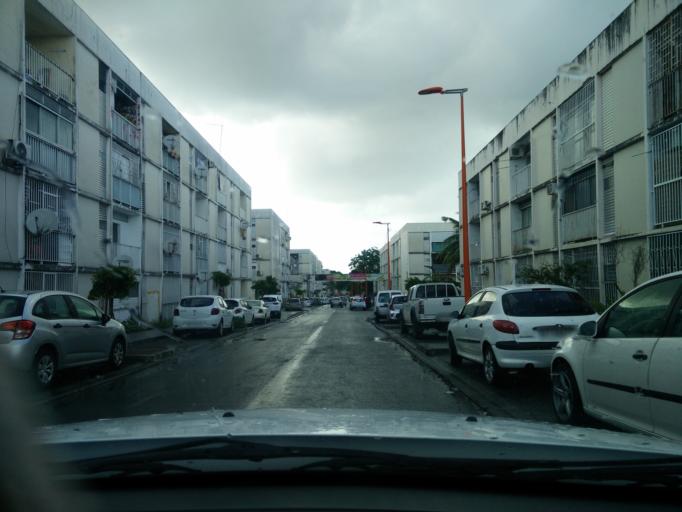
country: GP
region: Guadeloupe
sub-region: Guadeloupe
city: Pointe-a-Pitre
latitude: 16.2506
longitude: -61.5369
